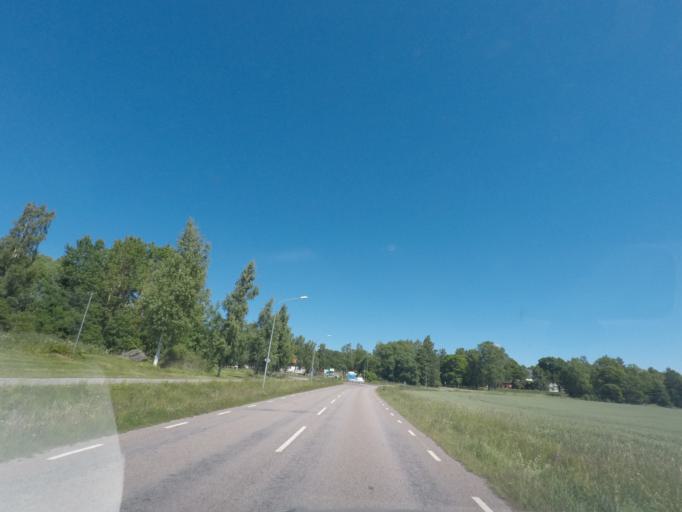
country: SE
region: Vaestmanland
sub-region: Vasteras
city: Tillberga
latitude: 59.6758
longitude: 16.7271
